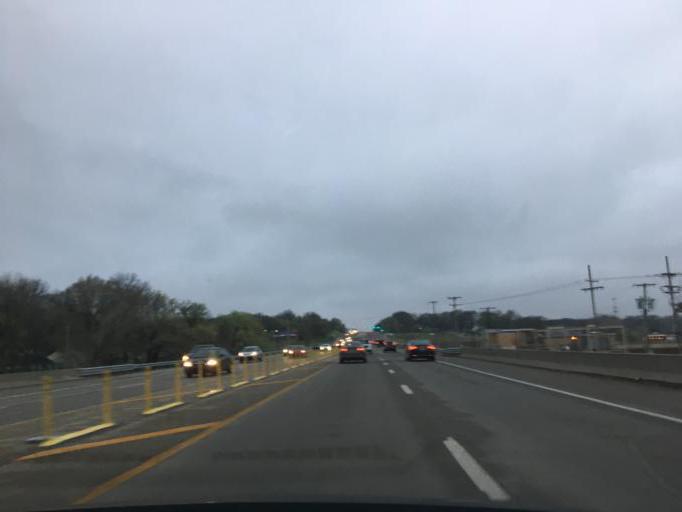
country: US
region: Kansas
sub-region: Johnson County
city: Fairway
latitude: 39.0247
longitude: -94.6383
